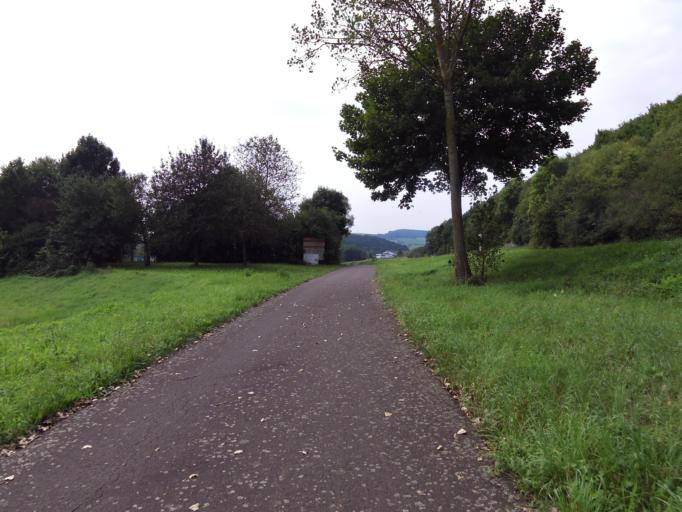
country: DE
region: Rheinland-Pfalz
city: Kalkofen
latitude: 49.7381
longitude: 7.8187
